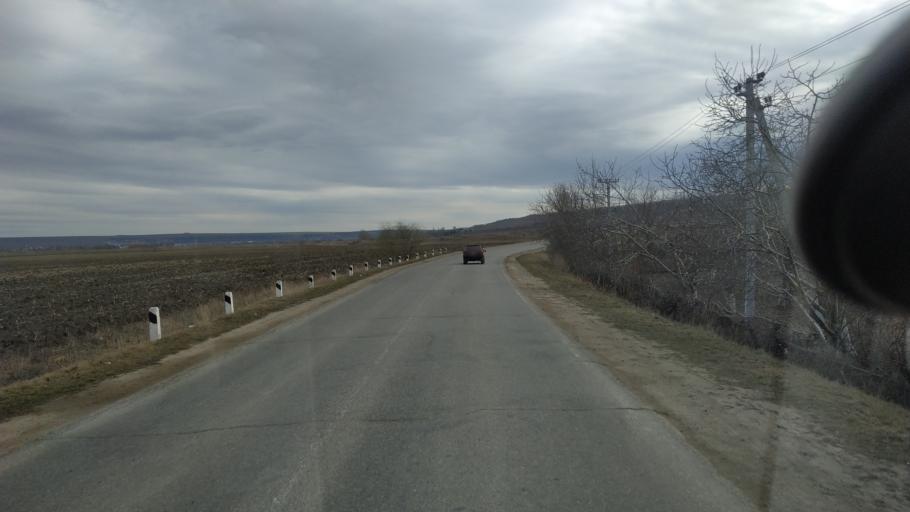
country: MD
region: Telenesti
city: Dubasari
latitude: 47.2553
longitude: 29.1354
